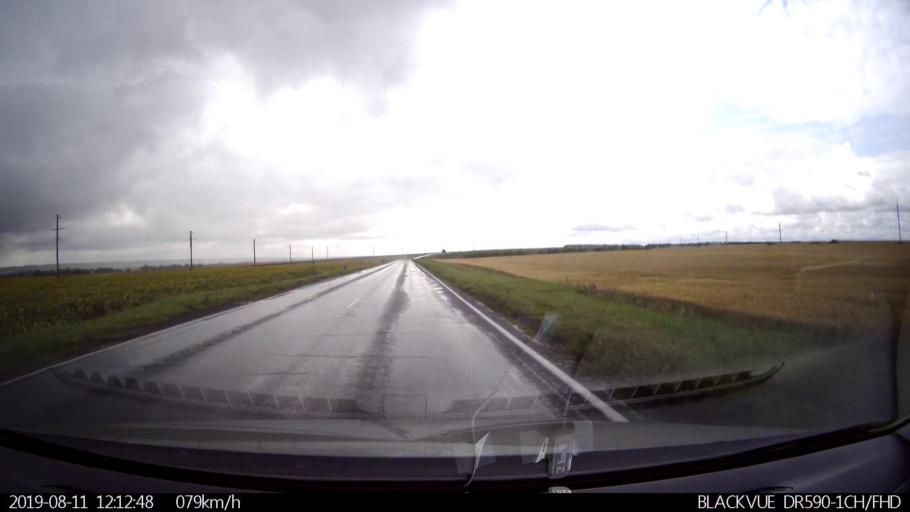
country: RU
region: Ulyanovsk
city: Silikatnyy
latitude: 53.9688
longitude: 47.9951
